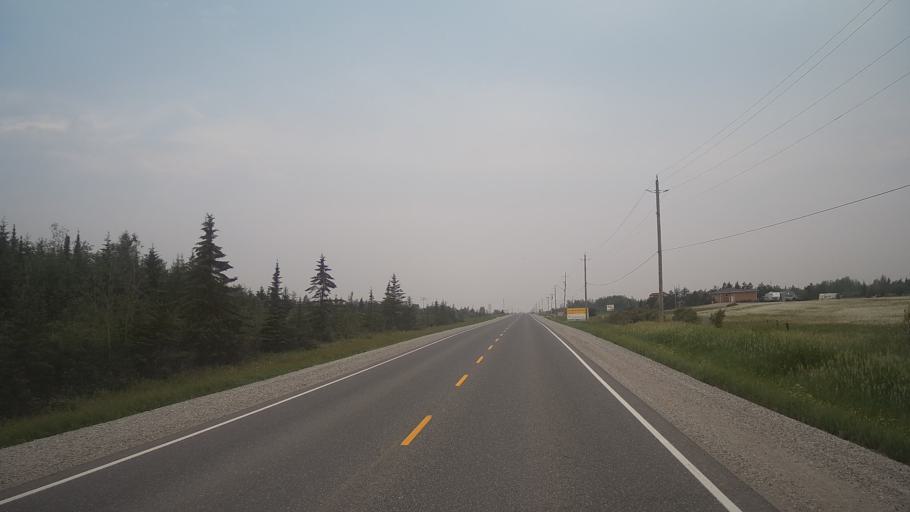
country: CA
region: Ontario
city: Hearst
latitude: 49.6809
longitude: -83.6104
